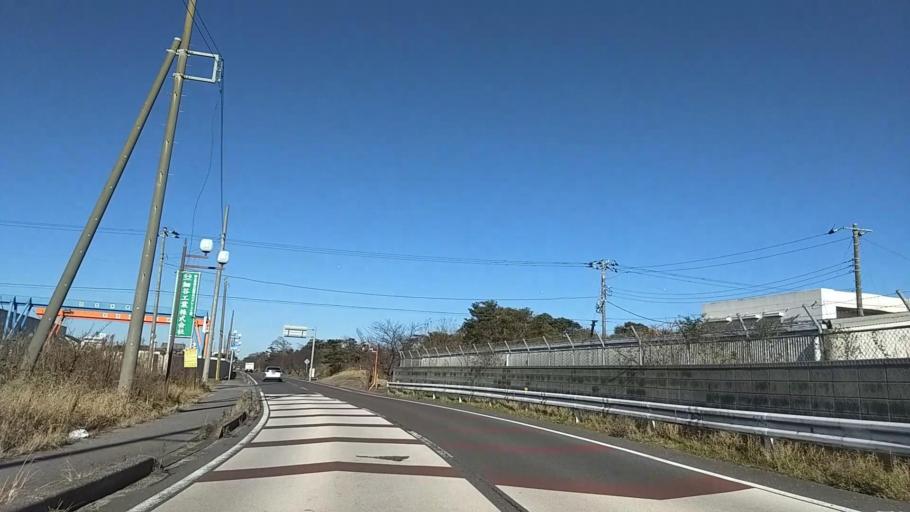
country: JP
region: Chiba
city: Mobara
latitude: 35.4206
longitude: 140.3929
